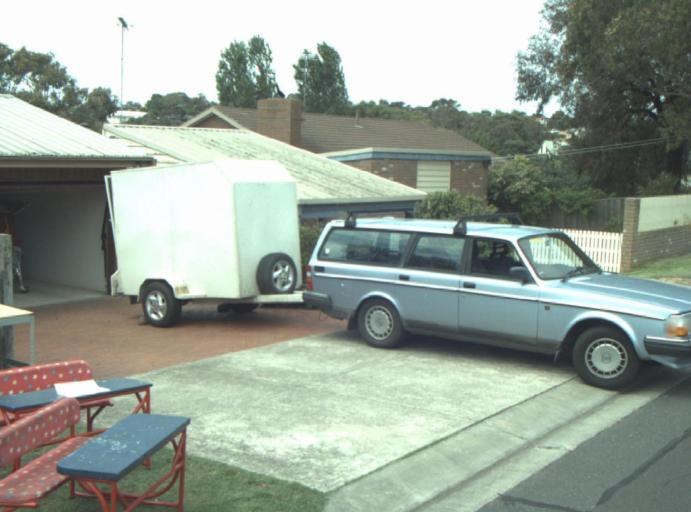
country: AU
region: Victoria
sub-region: Greater Geelong
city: Leopold
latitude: -38.2605
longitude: 144.5134
